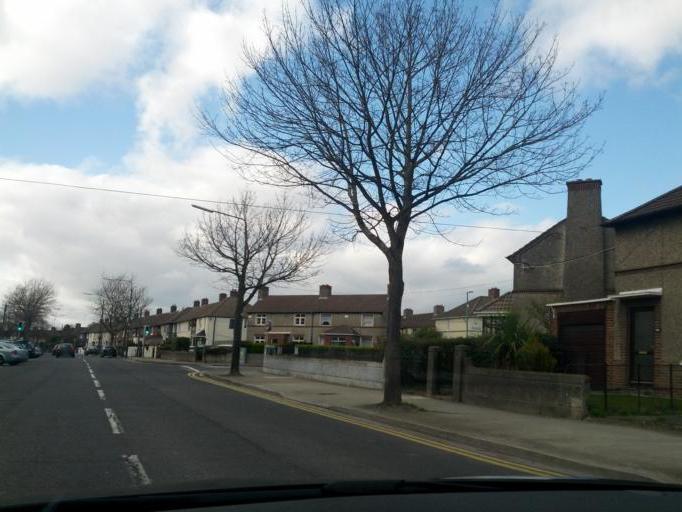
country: IE
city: Donnycarney
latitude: 53.3726
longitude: -6.2088
